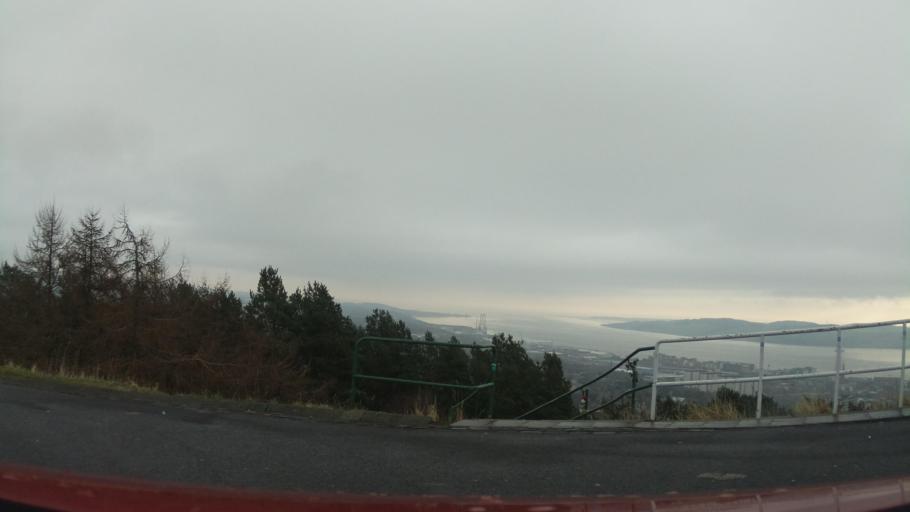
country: GB
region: Scotland
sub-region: Dundee City
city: Dundee
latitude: 56.4699
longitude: -2.9892
